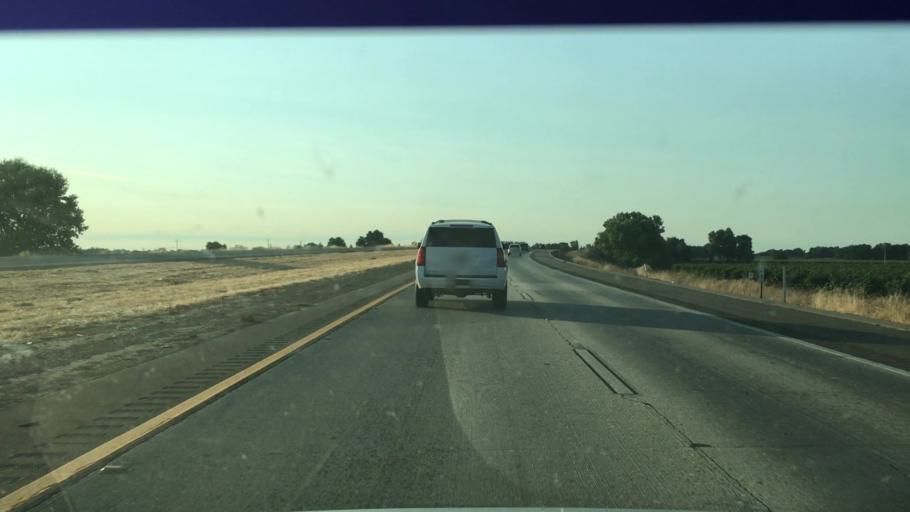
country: US
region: California
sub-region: San Joaquin County
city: Thornton
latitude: 38.2431
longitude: -121.4427
